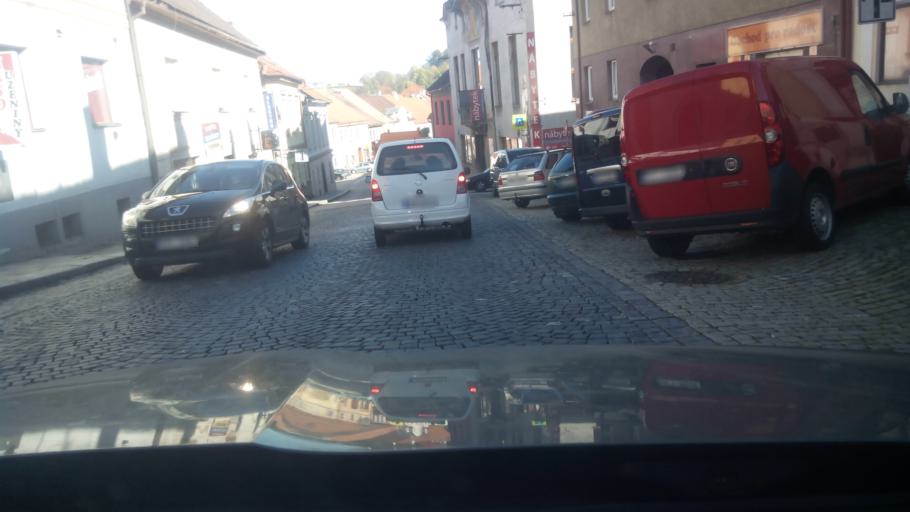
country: CZ
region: Jihocesky
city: Volyne
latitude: 49.1662
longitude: 13.8870
